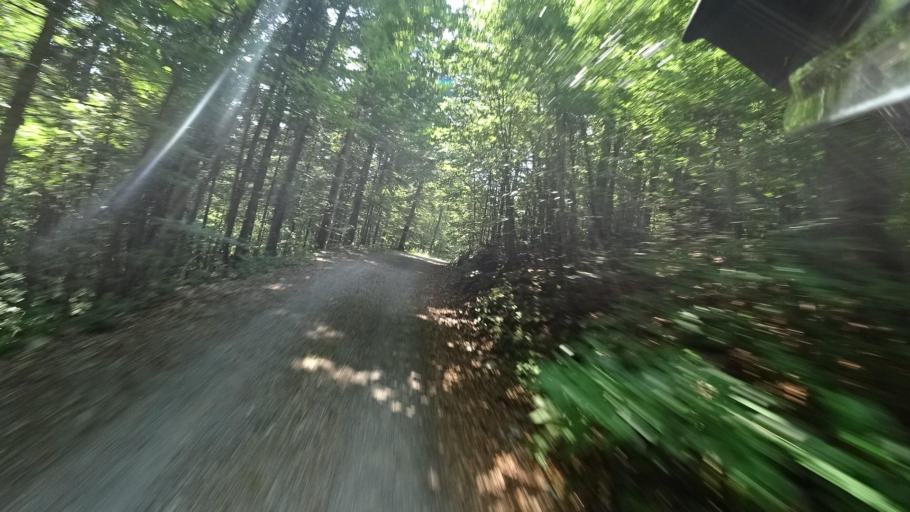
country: HR
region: Primorsko-Goranska
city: Vrbovsko
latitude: 45.2987
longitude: 15.1026
